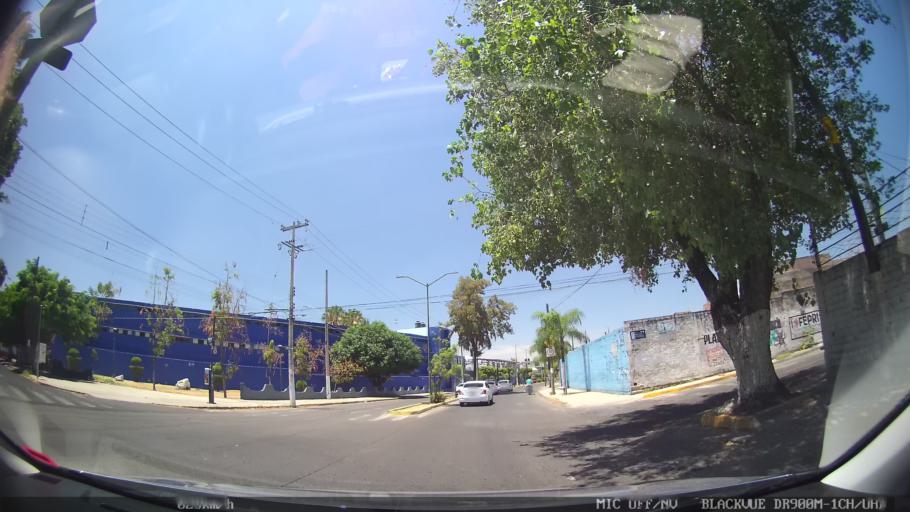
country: MX
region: Jalisco
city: Tlaquepaque
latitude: 20.6839
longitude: -103.2781
